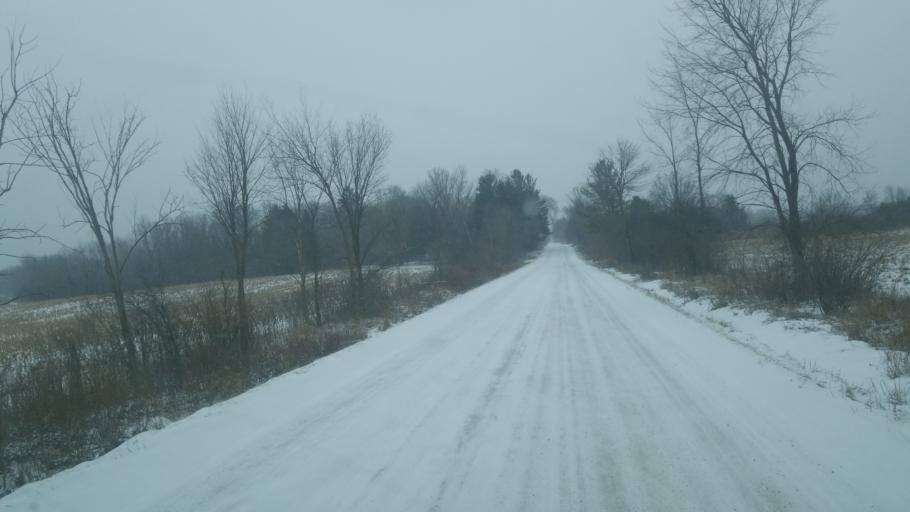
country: US
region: Michigan
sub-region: Osceola County
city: Reed City
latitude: 43.8464
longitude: -85.3940
